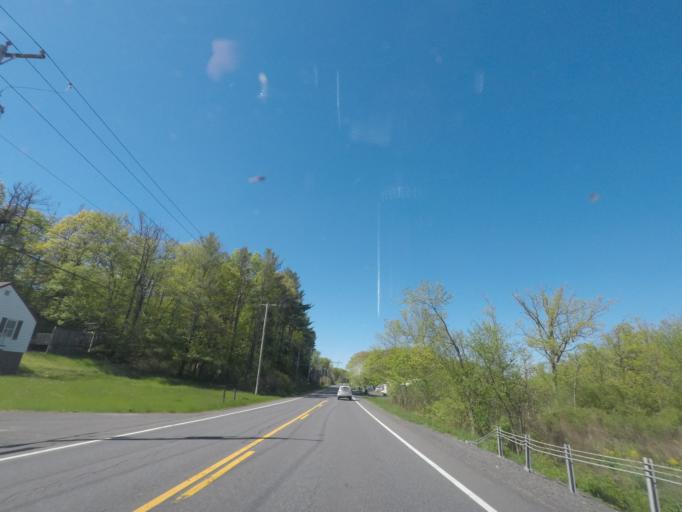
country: US
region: New York
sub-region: Greene County
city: Jefferson Heights
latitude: 42.2619
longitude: -73.8584
